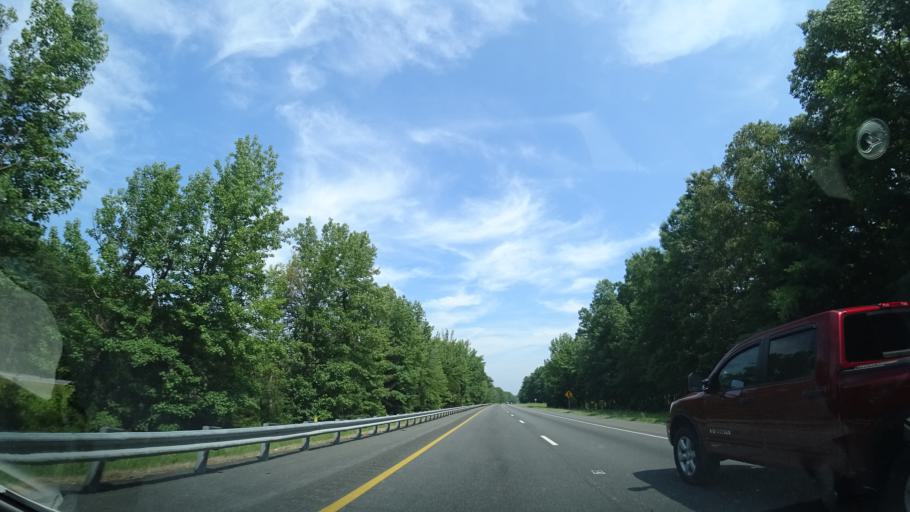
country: US
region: Virginia
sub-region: Louisa County
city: Louisa
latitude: 37.9394
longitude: -78.1070
